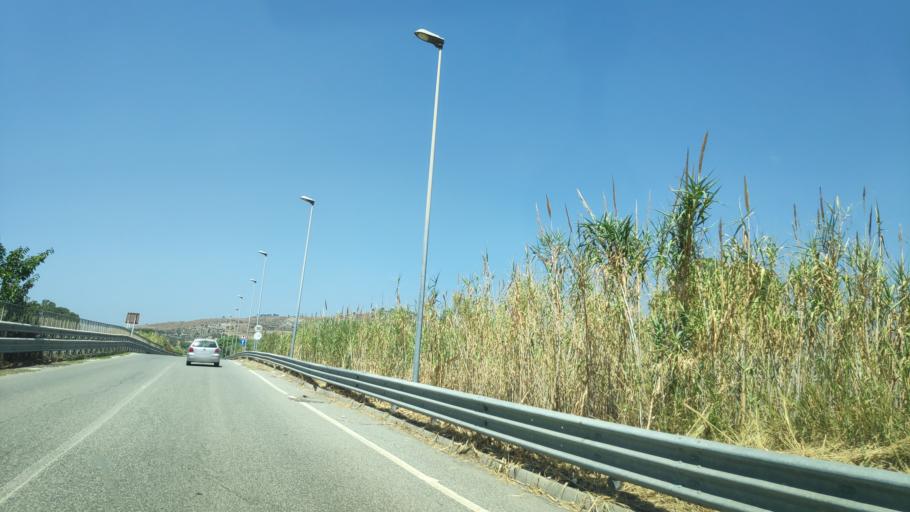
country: IT
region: Calabria
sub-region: Provincia di Reggio Calabria
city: Palizzi Marina
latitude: 37.9211
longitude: 15.9584
